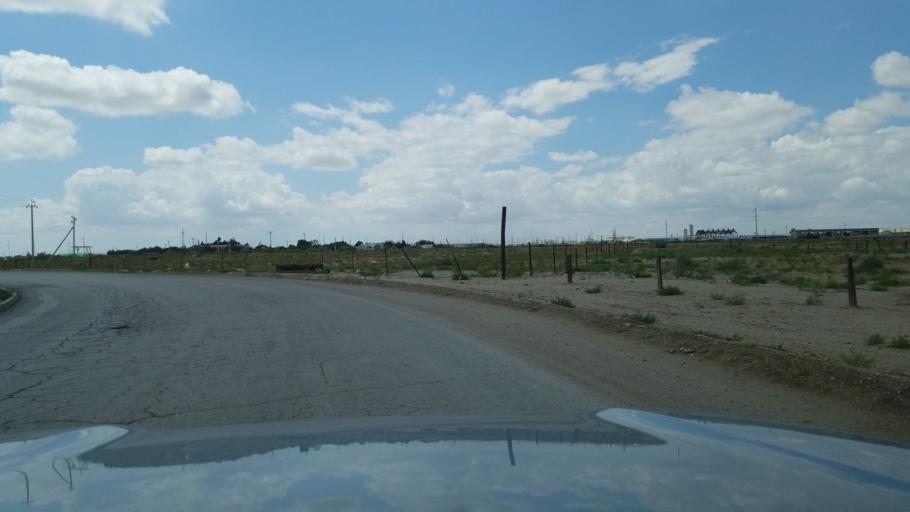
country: TM
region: Balkan
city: Balkanabat
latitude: 39.4980
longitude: 54.3528
